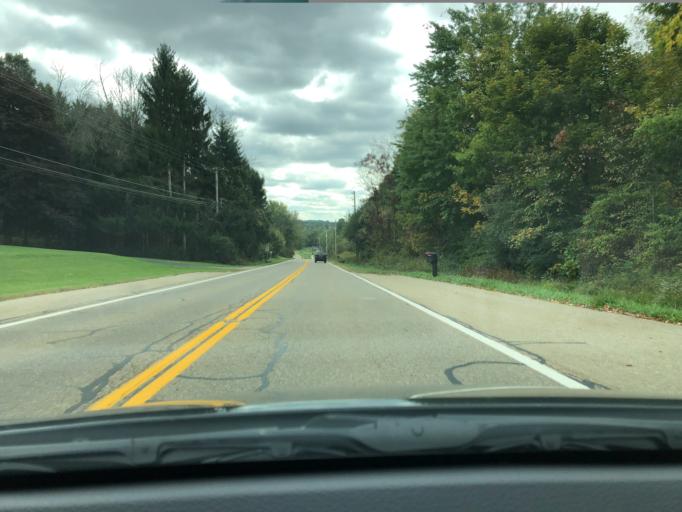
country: US
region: Ohio
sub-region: Stark County
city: Canal Fulton
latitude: 40.8750
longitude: -81.6063
